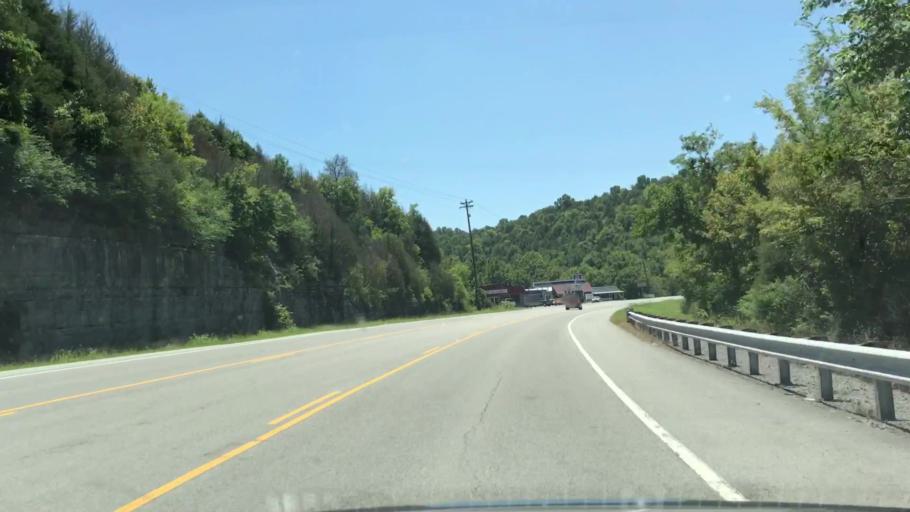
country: US
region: Tennessee
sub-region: Jackson County
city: Gainesboro
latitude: 36.3671
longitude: -85.6513
